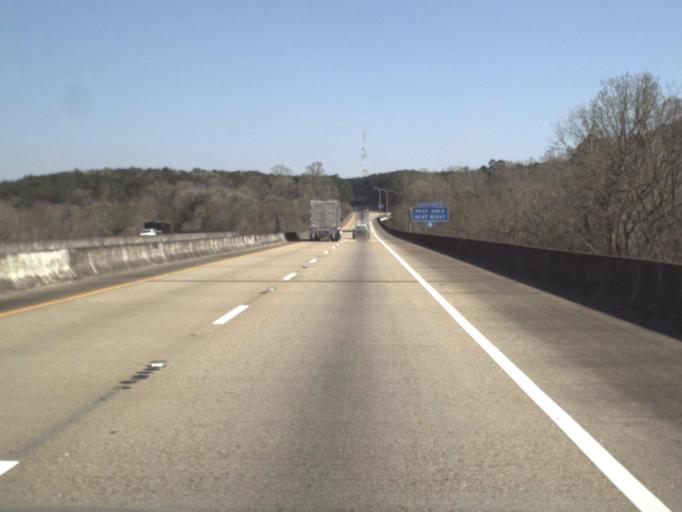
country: US
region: Florida
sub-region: Jackson County
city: Sneads
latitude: 30.6320
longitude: -84.9009
